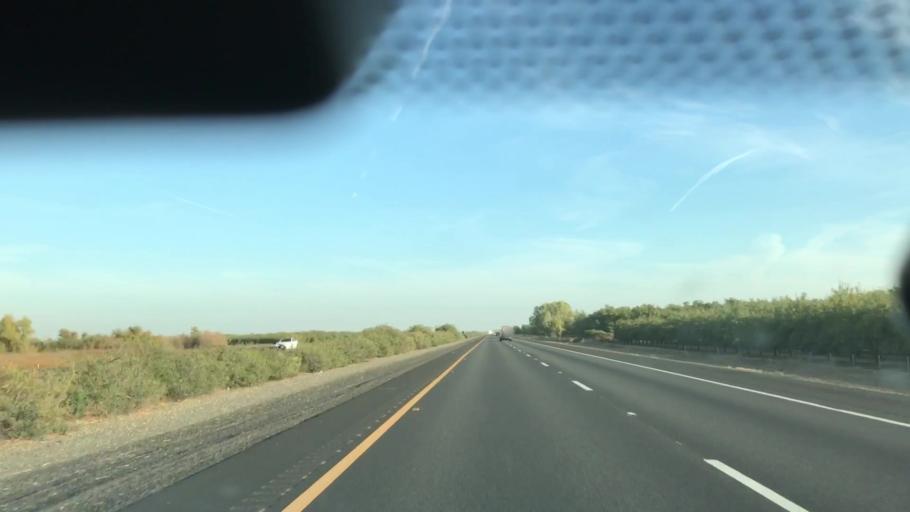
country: US
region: California
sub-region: Glenn County
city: Orland
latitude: 39.6371
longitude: -122.2041
